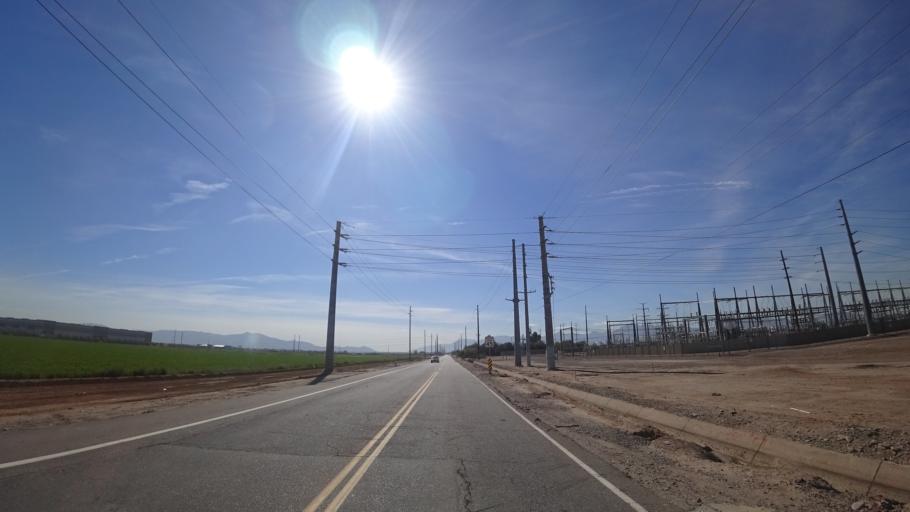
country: US
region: Arizona
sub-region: Maricopa County
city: Laveen
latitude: 33.4213
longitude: -112.1865
